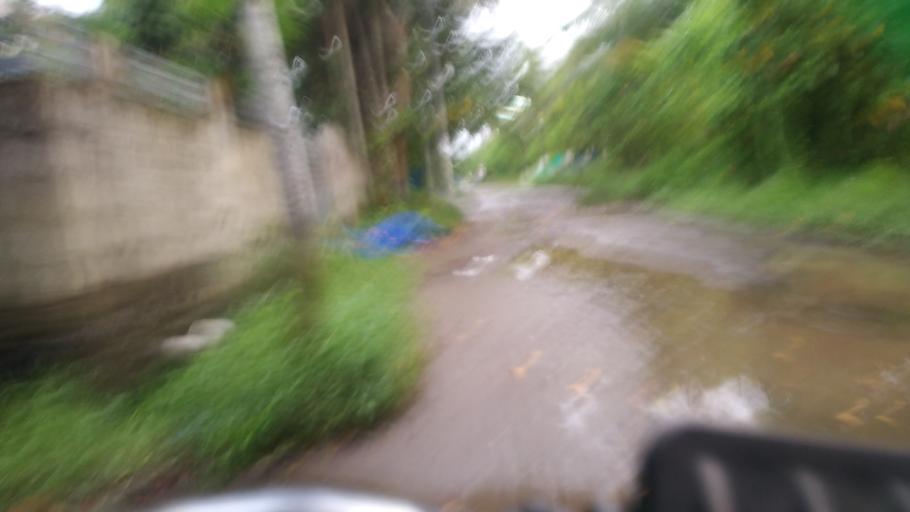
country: IN
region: Kerala
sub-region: Ernakulam
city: Cochin
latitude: 10.0117
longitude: 76.2176
